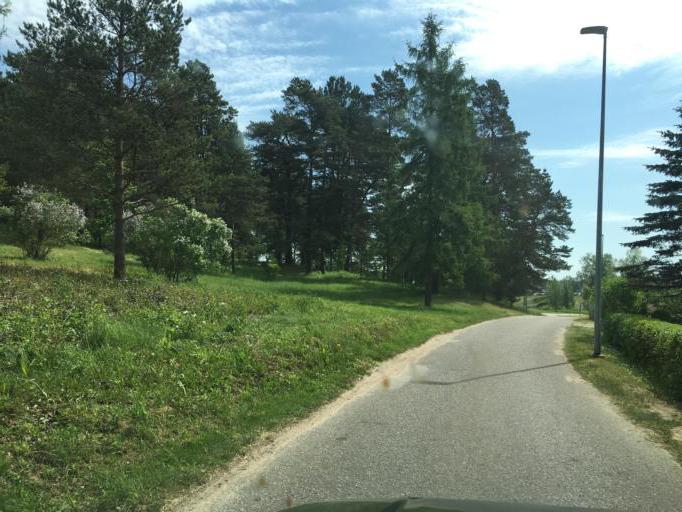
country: LV
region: Talsu Rajons
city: Valdemarpils
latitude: 57.3691
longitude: 22.5961
